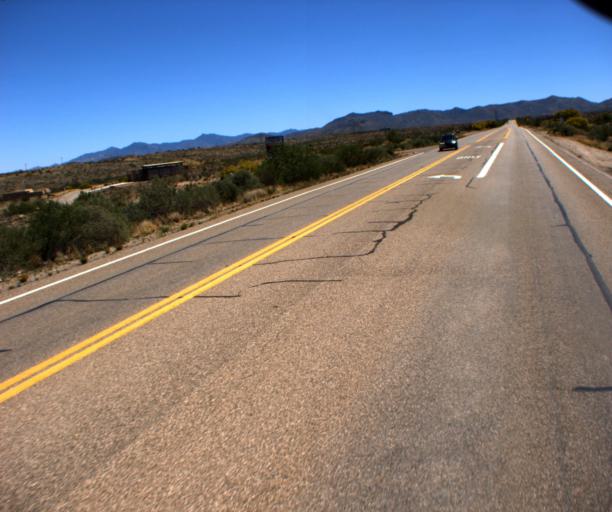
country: US
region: Arizona
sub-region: Pima County
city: Vail
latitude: 32.0001
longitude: -110.6880
